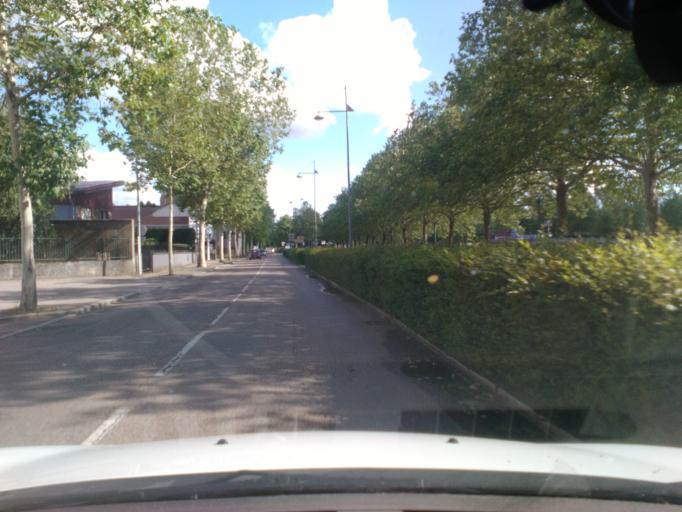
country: FR
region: Lorraine
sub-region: Departement des Vosges
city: Epinal
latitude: 48.1867
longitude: 6.4451
